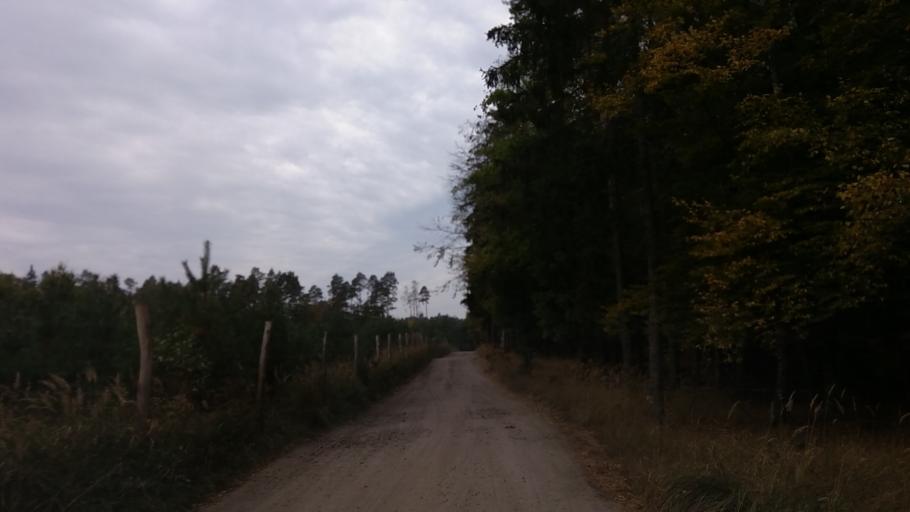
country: PL
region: West Pomeranian Voivodeship
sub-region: Powiat mysliborski
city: Barlinek
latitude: 52.9280
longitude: 15.2461
